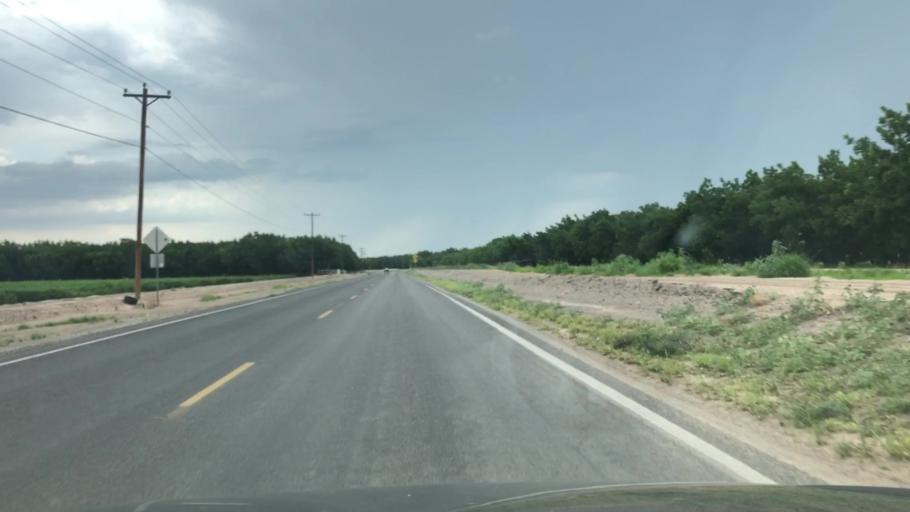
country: US
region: New Mexico
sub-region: Dona Ana County
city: La Union
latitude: 31.9878
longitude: -106.6501
